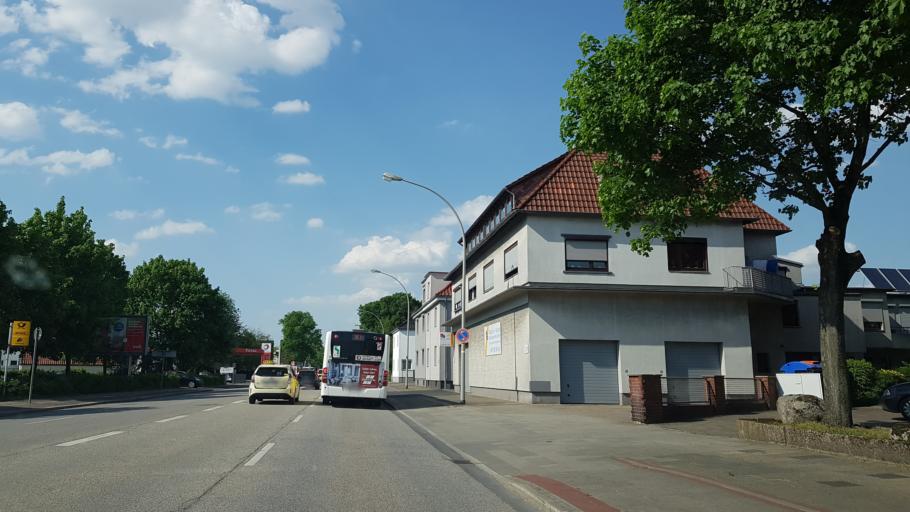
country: DE
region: Lower Saxony
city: Langen
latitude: 53.5866
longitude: 8.5979
